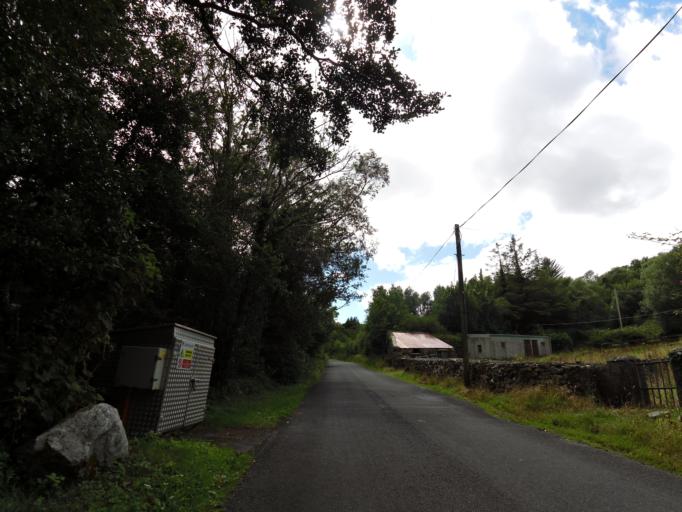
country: IE
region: Connaught
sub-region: County Galway
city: Oughterard
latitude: 53.4109
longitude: -9.3304
